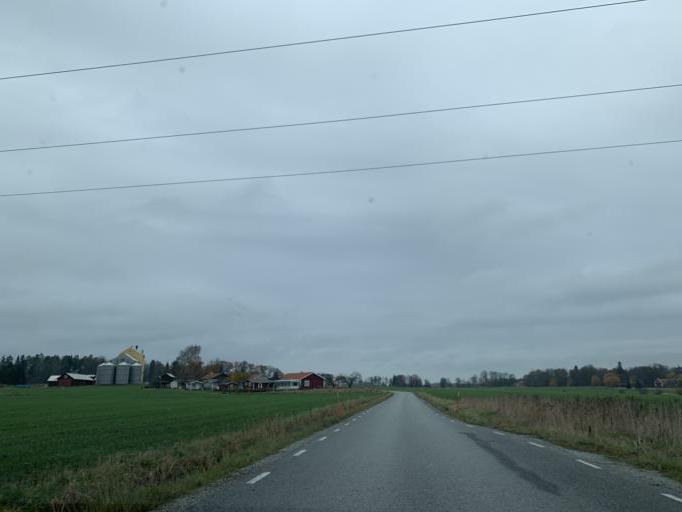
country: SE
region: Vaestmanland
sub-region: Vasteras
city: Skultuna
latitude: 59.7160
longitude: 16.4098
